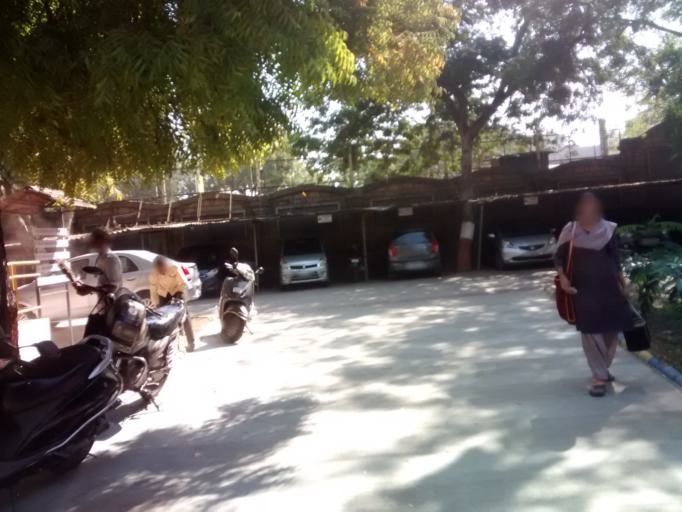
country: IN
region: Gujarat
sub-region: Ahmadabad
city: Ahmedabad
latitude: 23.0436
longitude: 72.5693
